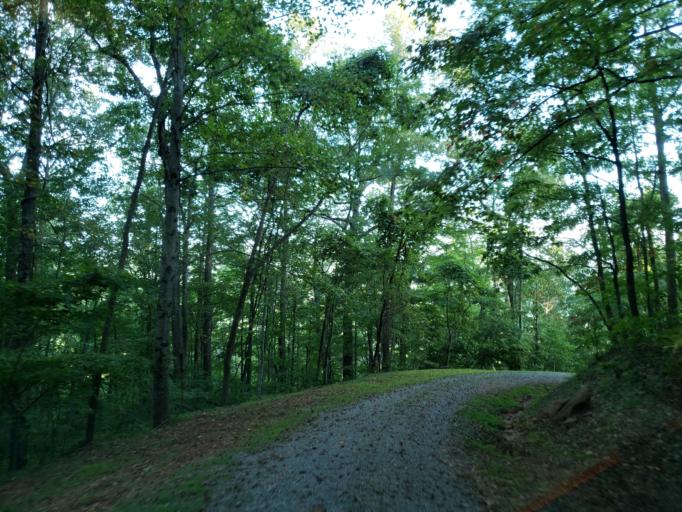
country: US
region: Georgia
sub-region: Fannin County
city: Blue Ridge
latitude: 34.6936
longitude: -84.2633
